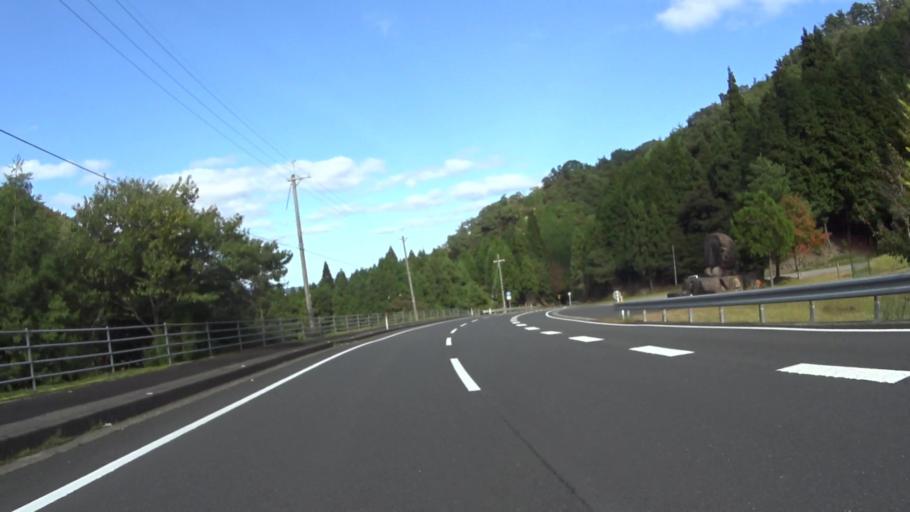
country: JP
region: Hyogo
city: Toyooka
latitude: 35.5337
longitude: 134.9777
